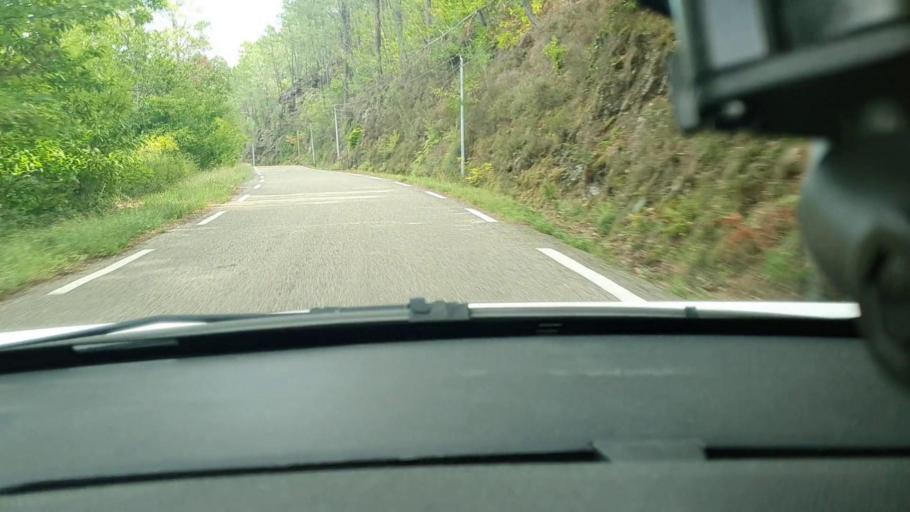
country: FR
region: Languedoc-Roussillon
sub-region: Departement du Gard
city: Besseges
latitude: 44.3059
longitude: 4.0539
